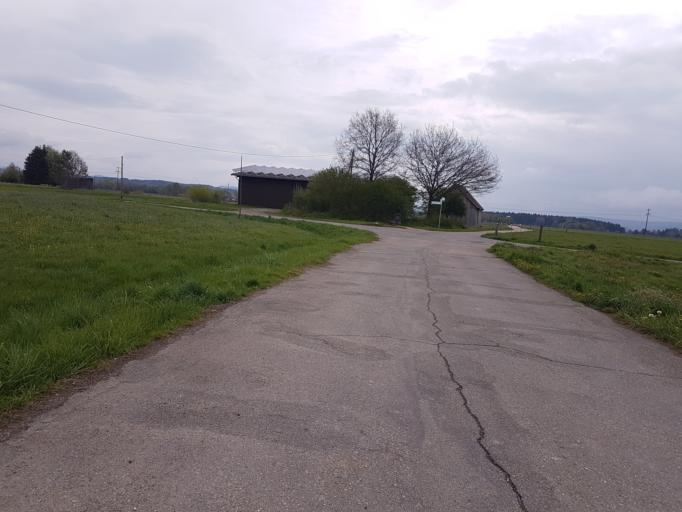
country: DE
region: Baden-Wuerttemberg
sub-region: Freiburg Region
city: Donaueschingen
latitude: 47.9400
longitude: 8.5066
